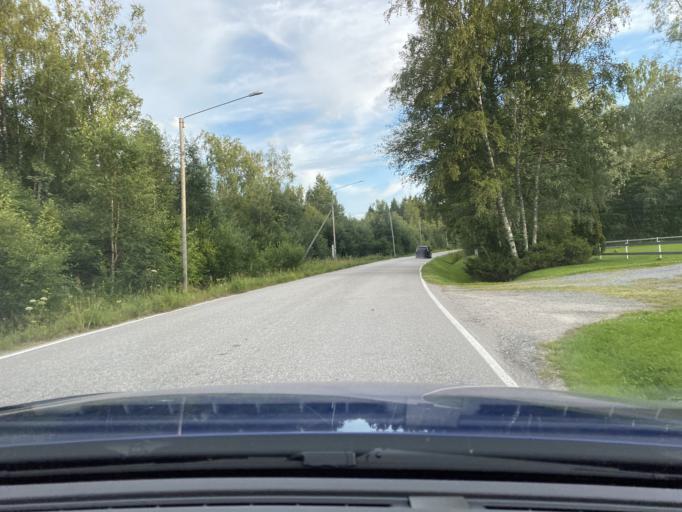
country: FI
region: Ostrobothnia
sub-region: Vaasa
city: Korsnaes
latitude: 62.9602
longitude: 21.1880
